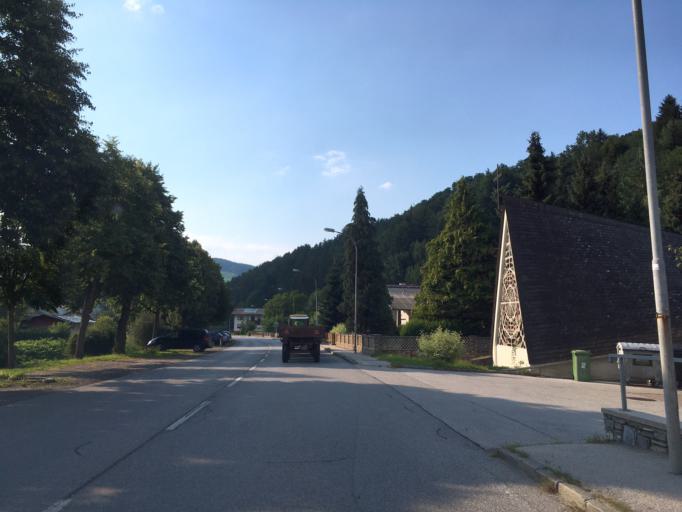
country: AT
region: Lower Austria
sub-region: Politischer Bezirk Neunkirchen
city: Grimmenstein
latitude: 47.6009
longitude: 16.1365
